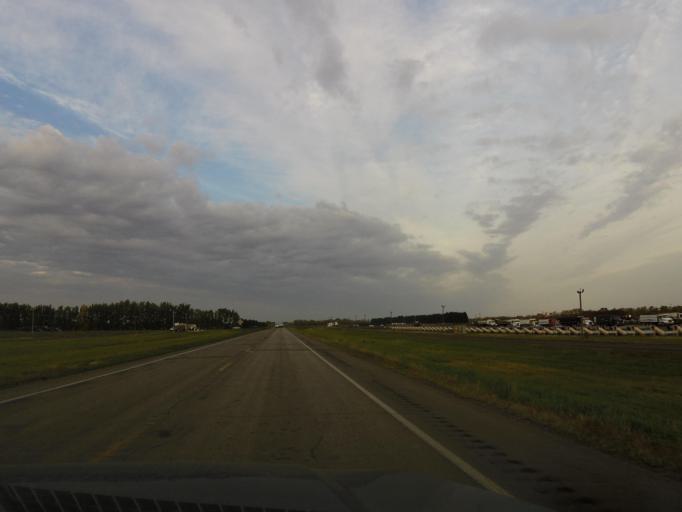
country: US
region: North Dakota
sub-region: Walsh County
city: Grafton
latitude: 48.6010
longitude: -97.4527
